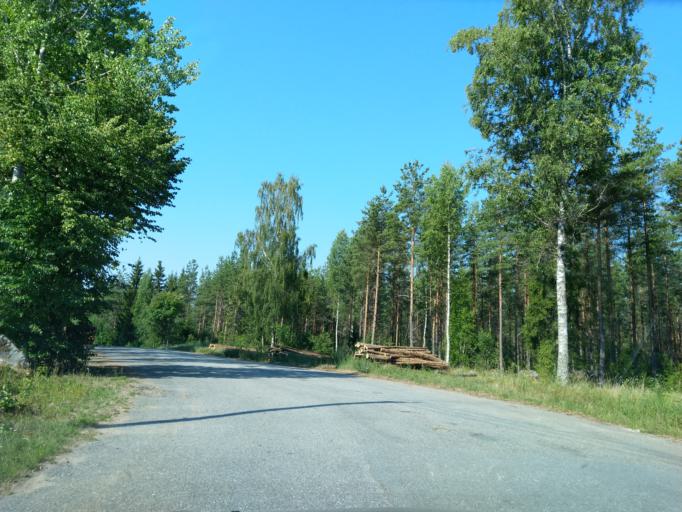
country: FI
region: Satakunta
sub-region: Pori
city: Pomarkku
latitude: 61.7202
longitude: 22.0523
